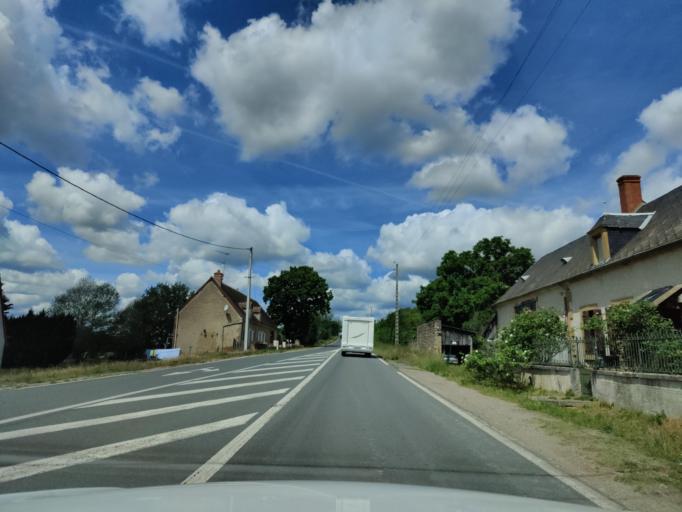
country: FR
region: Centre
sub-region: Departement du Cher
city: Saint-Amand-Montrond
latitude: 46.6533
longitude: 2.5800
